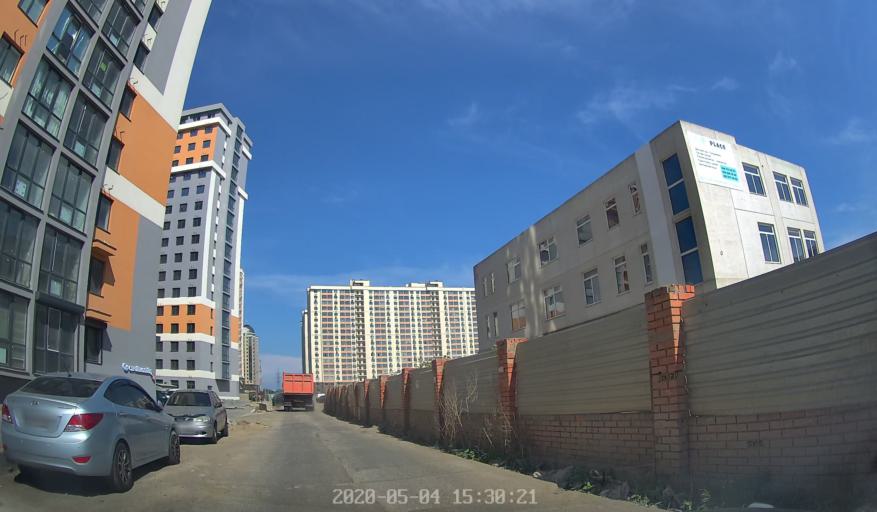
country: NE
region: Zinder
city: Mirriah
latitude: 13.9141
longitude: 9.2114
